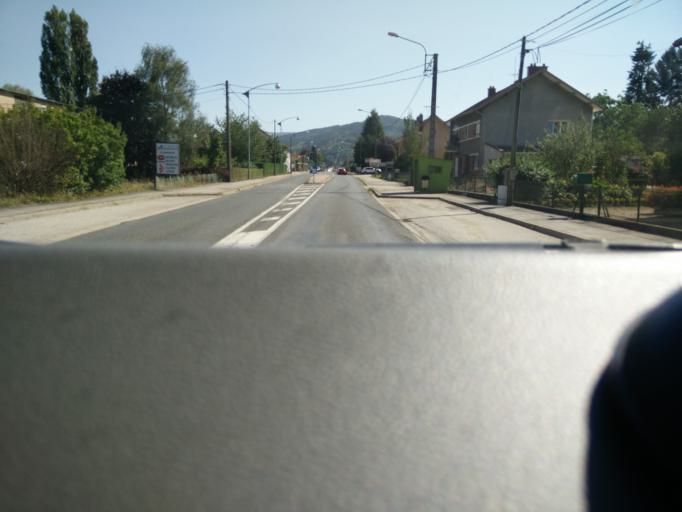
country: FR
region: Lorraine
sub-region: Departement des Vosges
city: Anould
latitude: 48.1979
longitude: 6.9471
